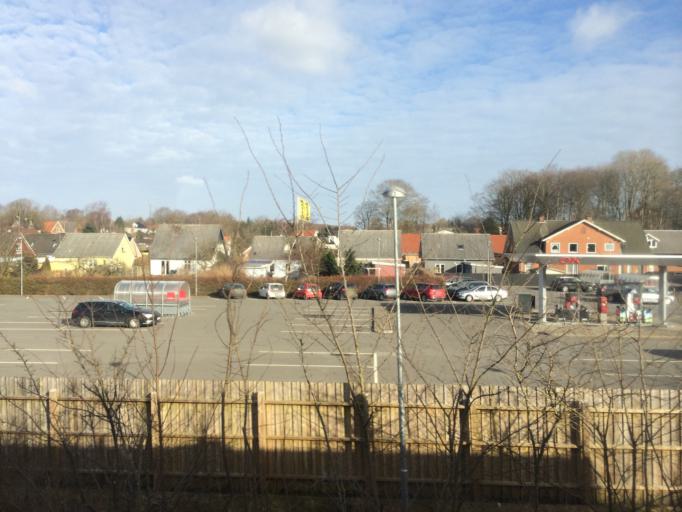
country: DK
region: South Denmark
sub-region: Vejle Kommune
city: Give
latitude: 55.8445
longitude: 9.2317
